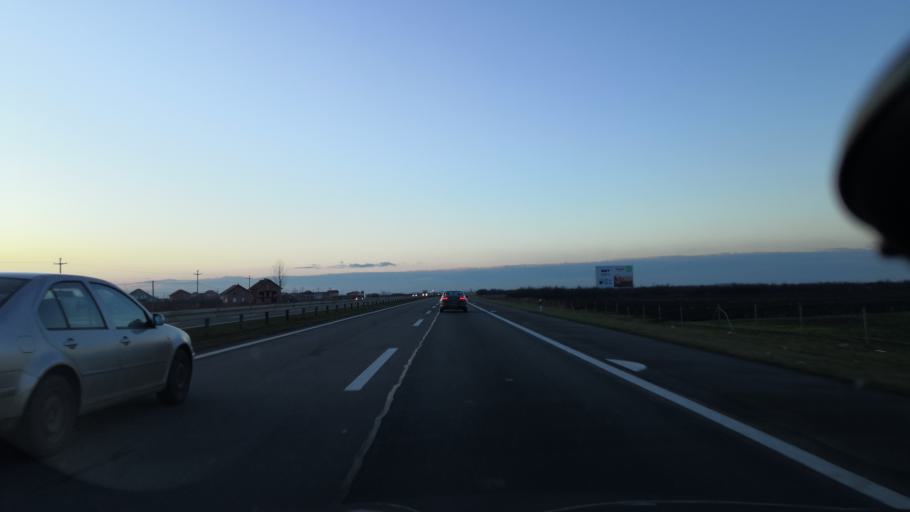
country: RS
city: Ugrinovci
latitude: 44.8578
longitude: 20.1650
